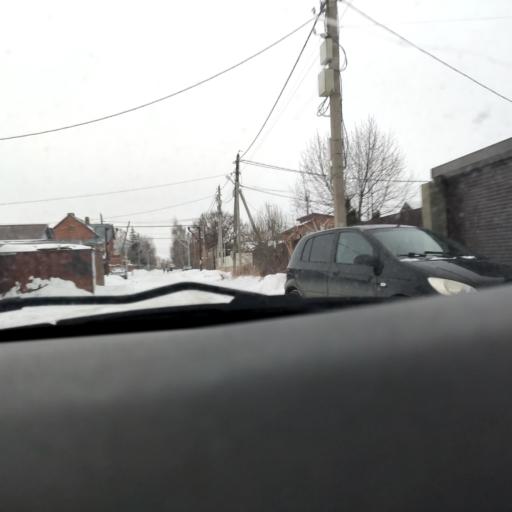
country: RU
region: Samara
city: Tol'yatti
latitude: 53.5080
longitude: 49.2445
